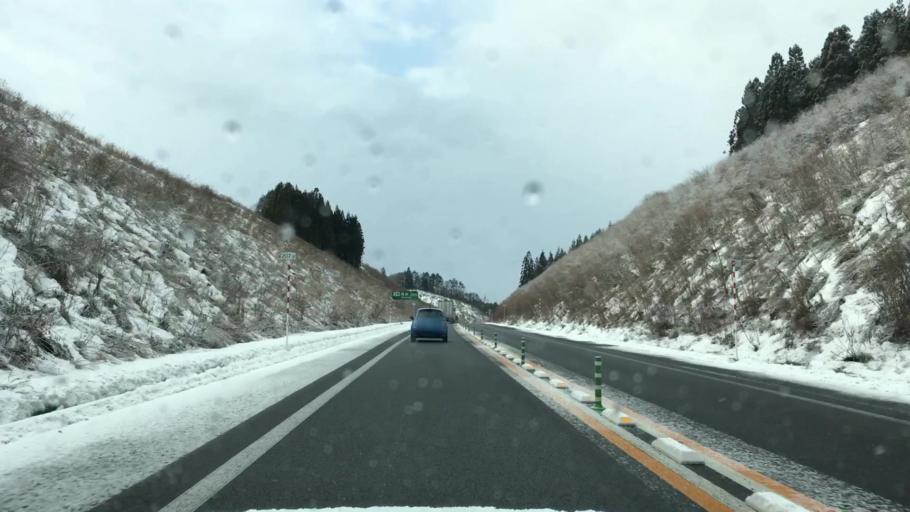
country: JP
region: Akita
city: Takanosu
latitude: 40.2138
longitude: 140.4198
